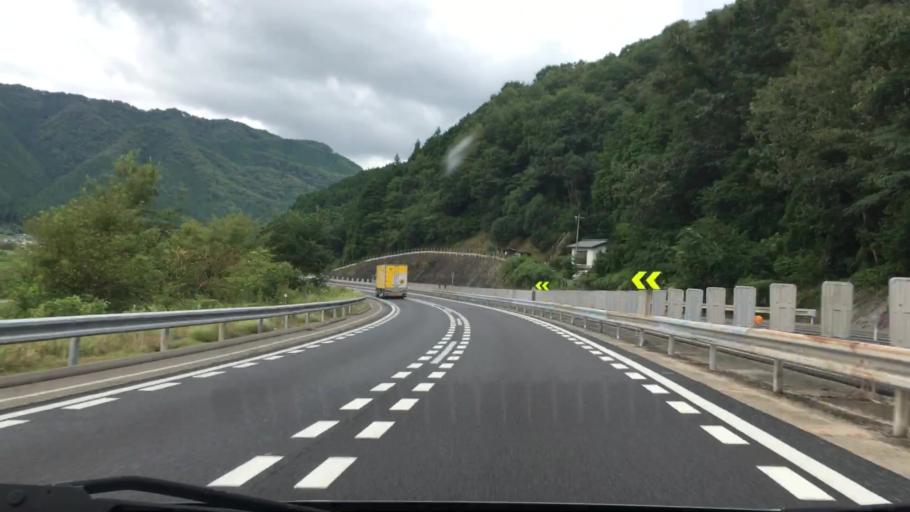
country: JP
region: Okayama
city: Takahashi
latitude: 34.9886
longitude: 133.7150
